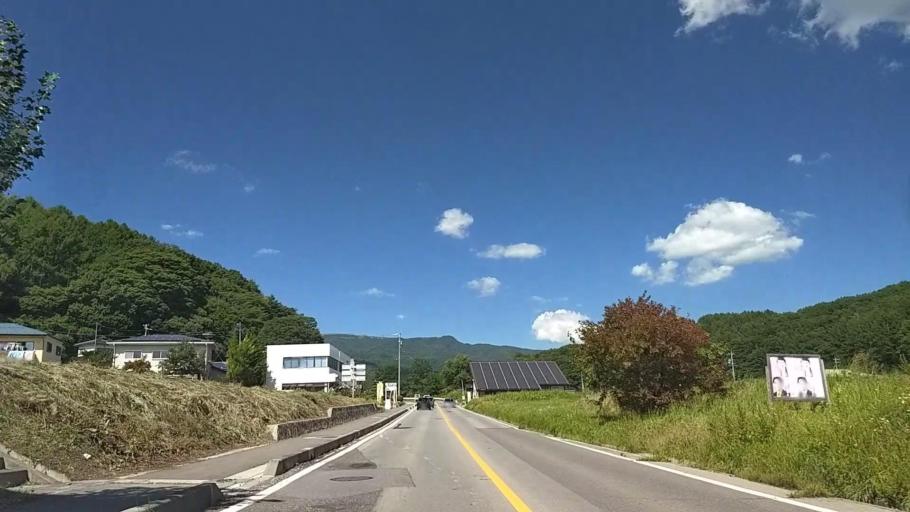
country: JP
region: Nagano
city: Chino
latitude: 36.0165
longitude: 138.1761
